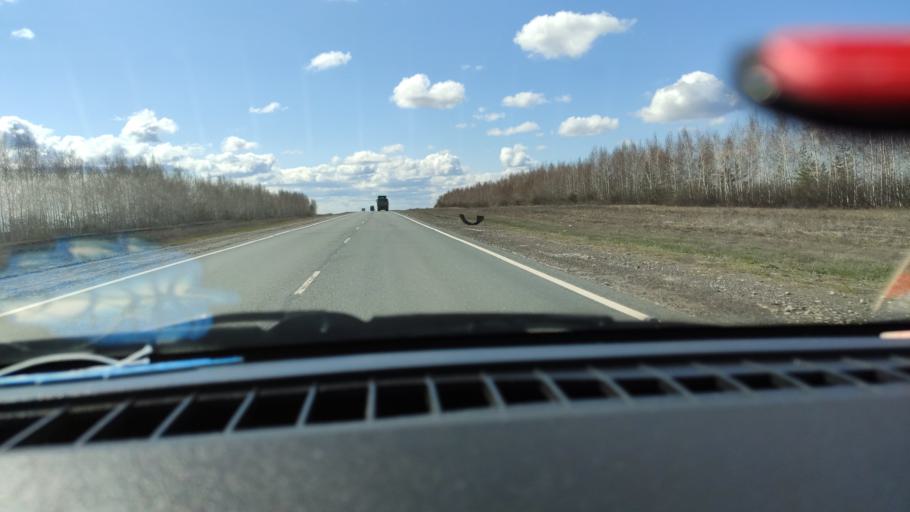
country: RU
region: Saratov
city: Dukhovnitskoye
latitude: 52.8104
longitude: 48.2290
